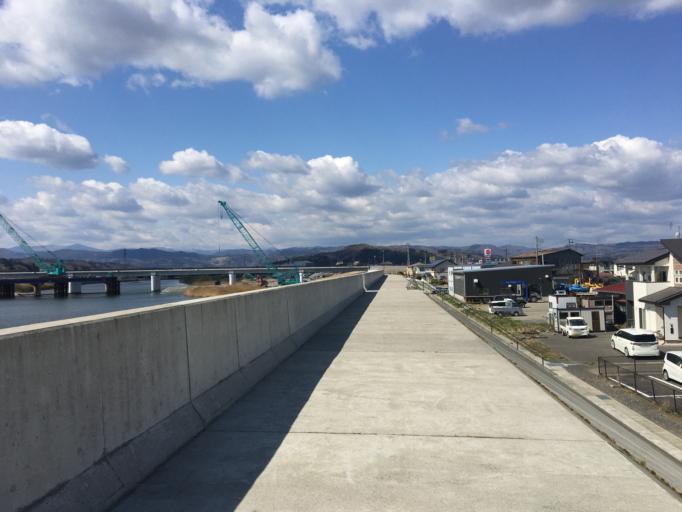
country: JP
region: Aomori
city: Hachinohe
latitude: 40.2003
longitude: 141.7924
